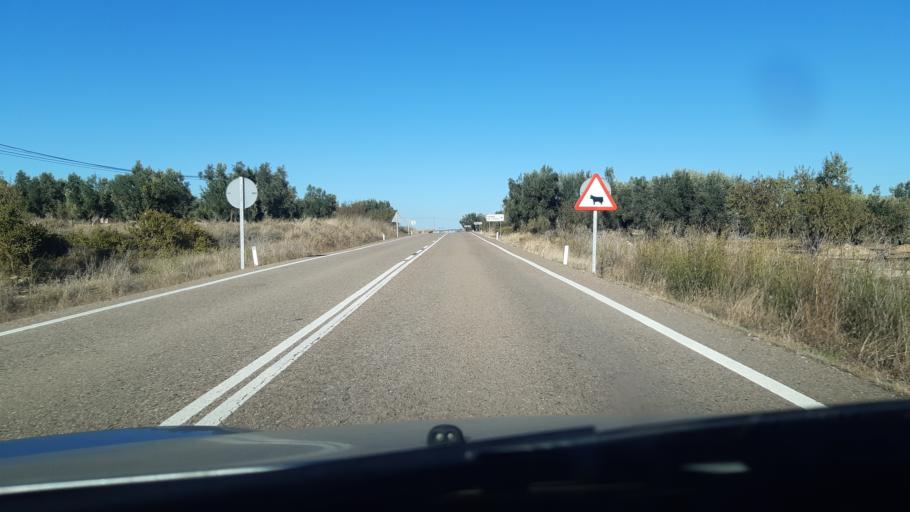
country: ES
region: Aragon
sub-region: Provincia de Teruel
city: Torre del Compte
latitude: 40.9263
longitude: 0.0812
